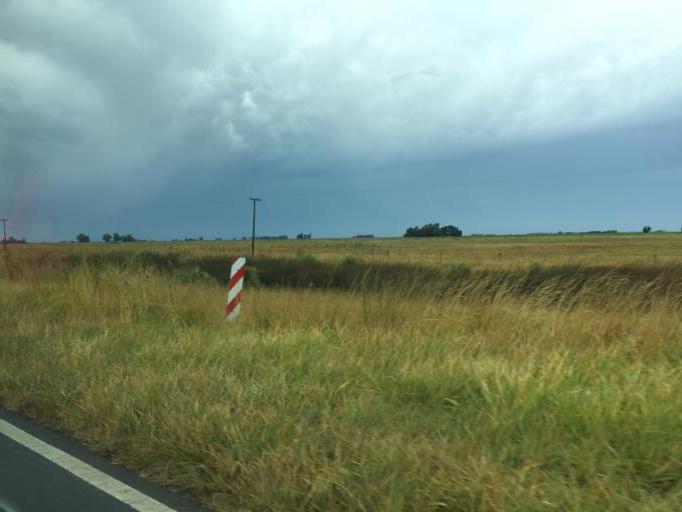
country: AR
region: Buenos Aires
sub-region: Partido de Rauch
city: Rauch
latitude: -36.9037
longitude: -58.9884
